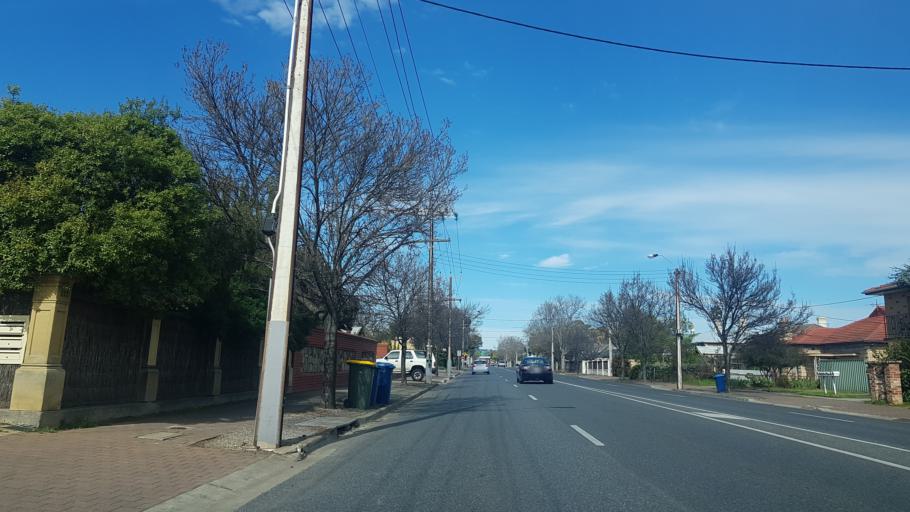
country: AU
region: South Australia
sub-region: Unley
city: Millswood
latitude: -34.9608
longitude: 138.5904
